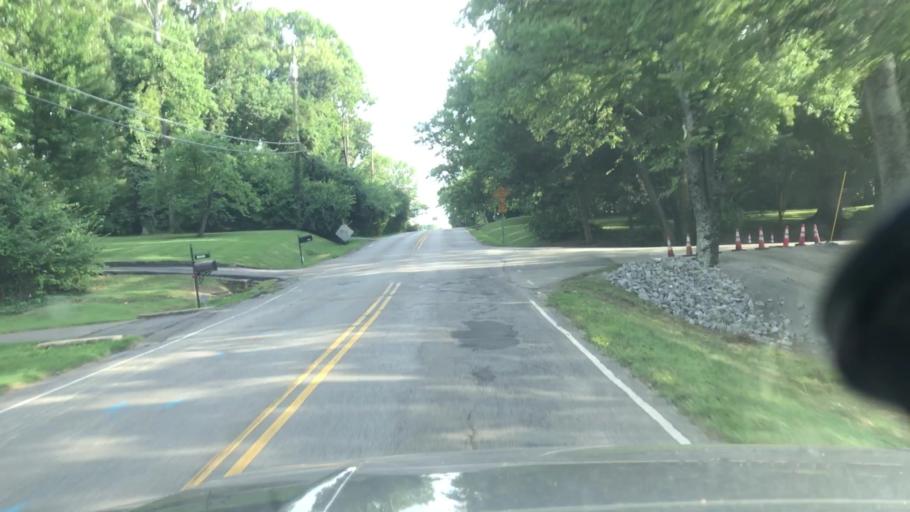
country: US
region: Tennessee
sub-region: Davidson County
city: Belle Meade
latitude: 36.0997
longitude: -86.8387
